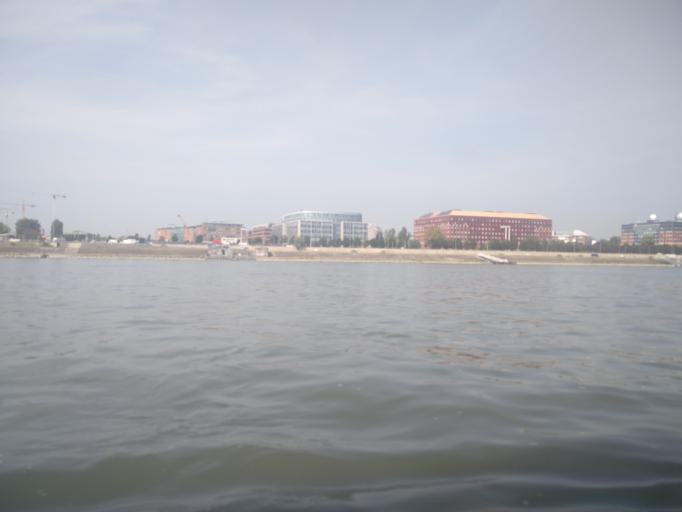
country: HU
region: Budapest
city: Budapest IX. keruelet
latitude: 47.4706
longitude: 19.0688
